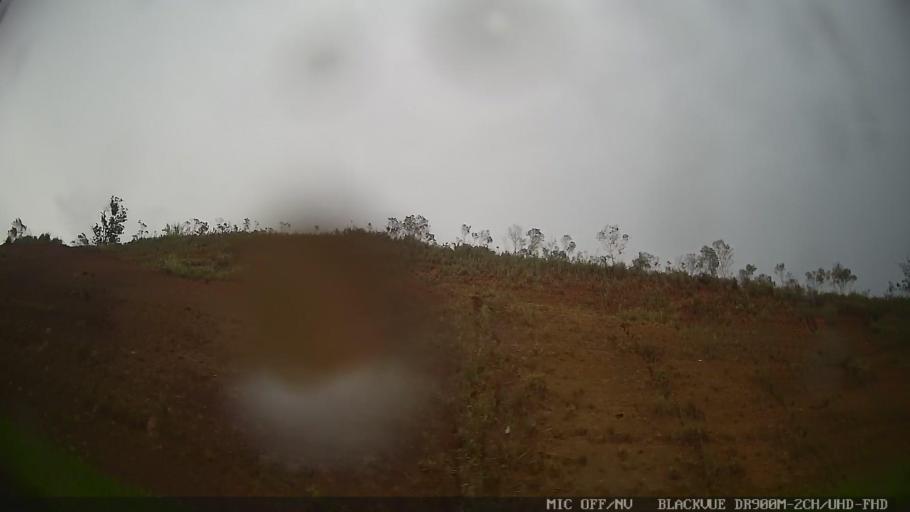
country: BR
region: Sao Paulo
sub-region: Pedreira
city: Pedreira
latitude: -22.7331
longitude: -46.8632
